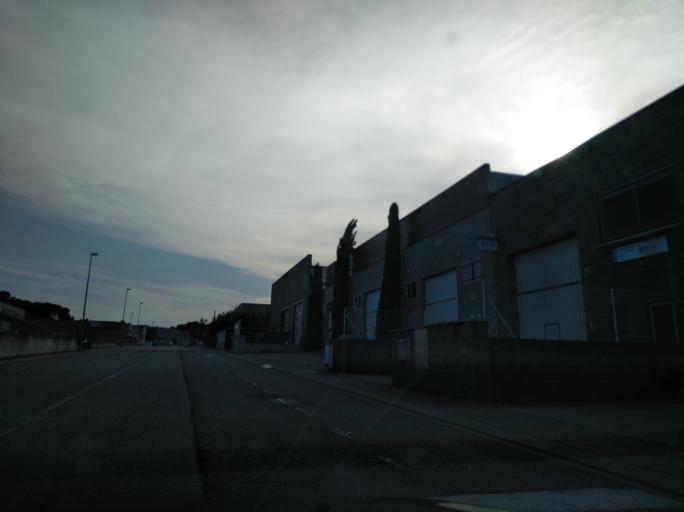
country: ES
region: Catalonia
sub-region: Provincia de Girona
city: Vilablareix
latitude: 41.9434
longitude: 2.7811
